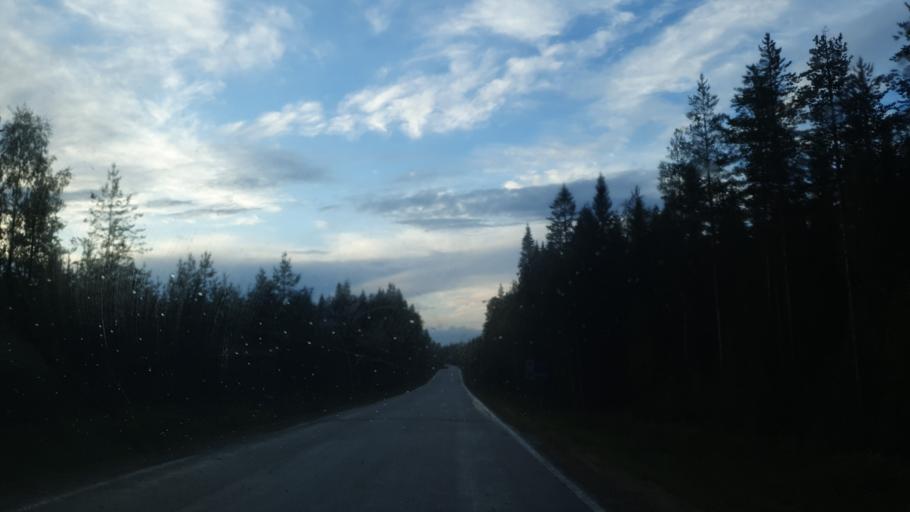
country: FI
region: North Karelia
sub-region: Pielisen Karjala
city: Lieksa
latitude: 63.7404
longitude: 29.8567
